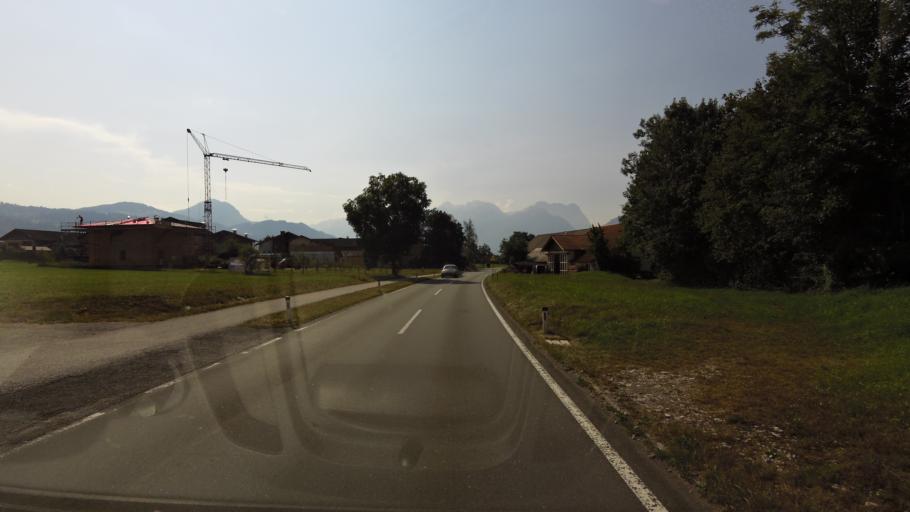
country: AT
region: Salzburg
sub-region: Politischer Bezirk Hallein
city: Kuchl
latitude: 47.6457
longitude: 13.1331
